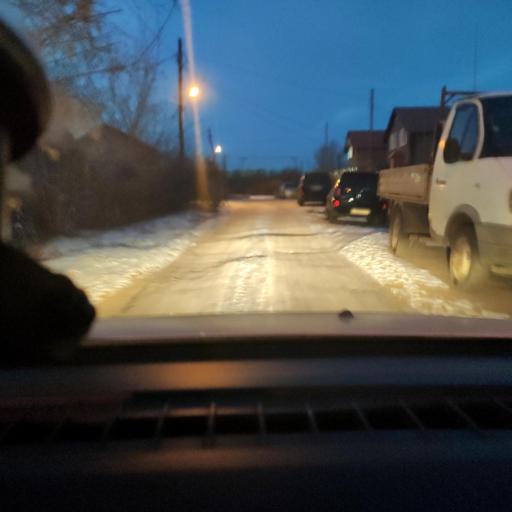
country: RU
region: Samara
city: Smyshlyayevka
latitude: 53.2560
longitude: 50.3556
